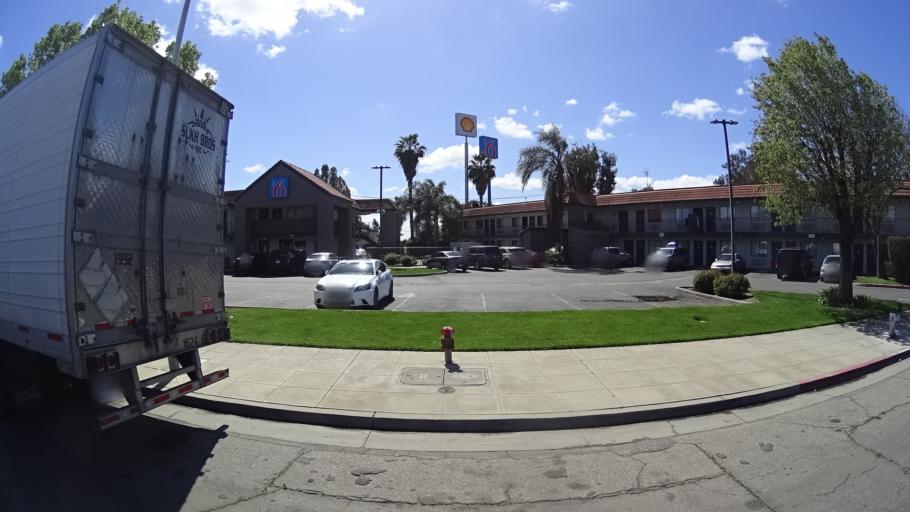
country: US
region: California
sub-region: Fresno County
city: West Park
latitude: 36.8092
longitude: -119.8861
